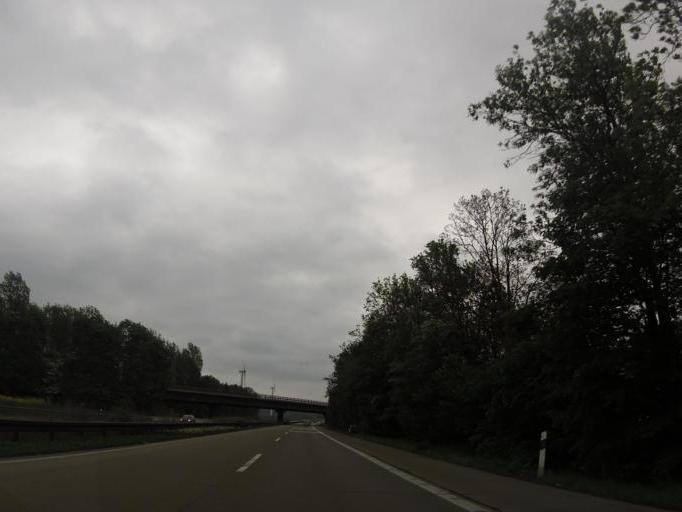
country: DE
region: Lower Saxony
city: Holle
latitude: 52.0876
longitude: 10.1798
